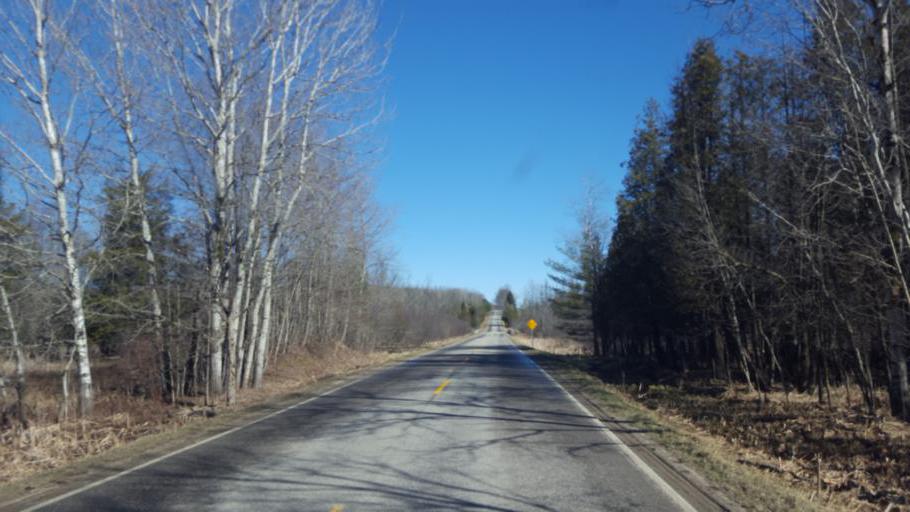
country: US
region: Michigan
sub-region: Isabella County
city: Lake Isabella
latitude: 43.5410
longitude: -85.0262
